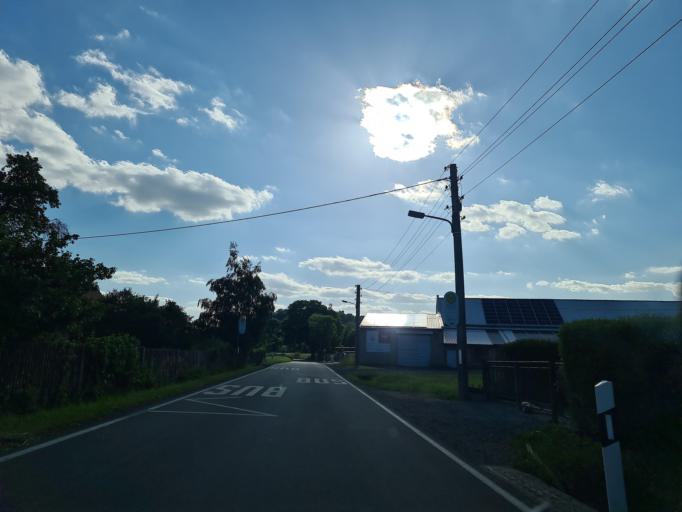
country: DE
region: Saxony
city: Weischlitz
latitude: 50.4905
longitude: 12.0760
